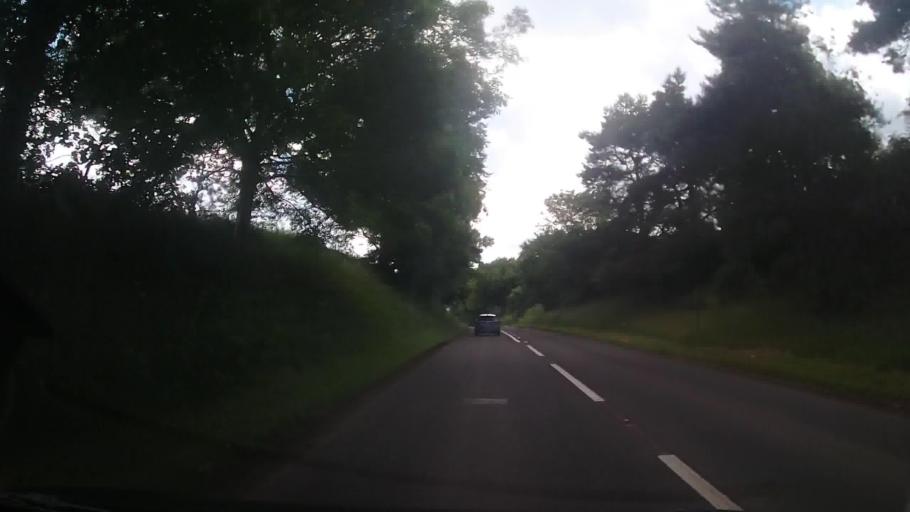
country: GB
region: England
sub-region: Shropshire
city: Ellesmere
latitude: 52.8989
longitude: -2.9235
